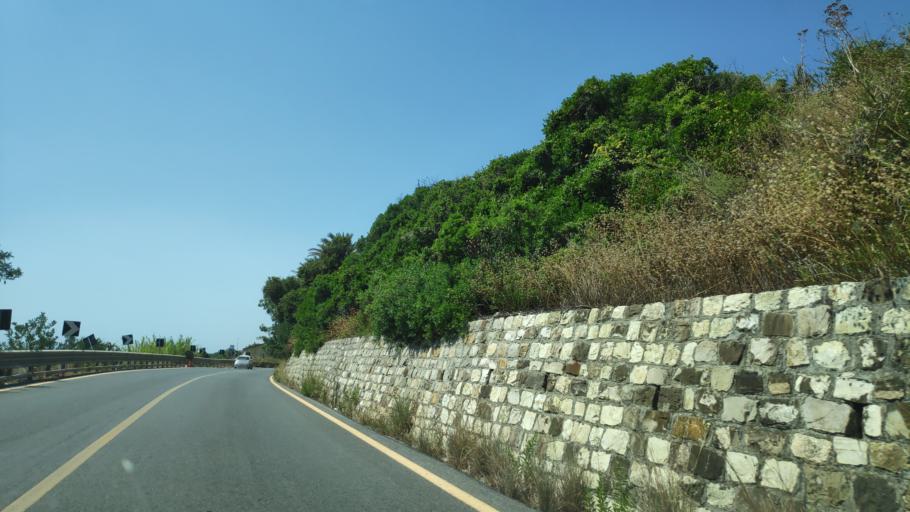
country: IT
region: Calabria
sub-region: Provincia di Reggio Calabria
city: Africo Nuovo
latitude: 38.0235
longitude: 16.1383
